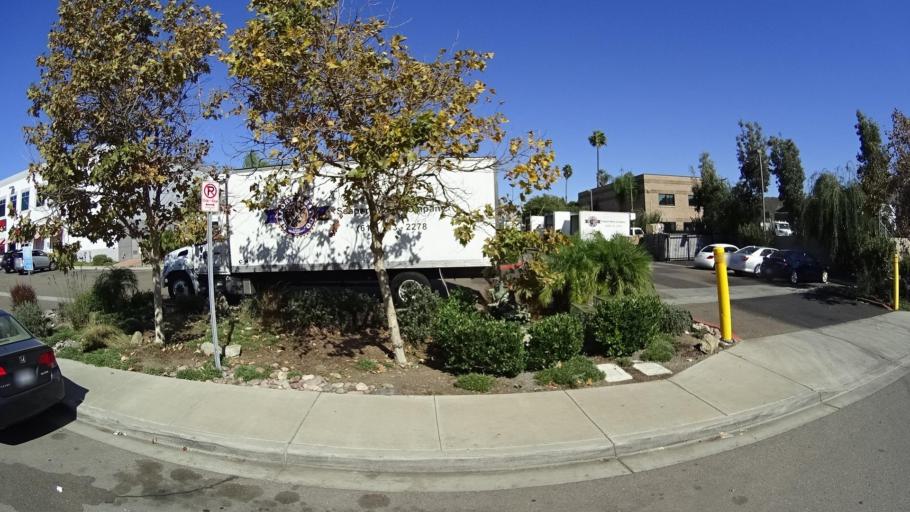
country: US
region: California
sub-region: San Diego County
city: La Presa
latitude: 32.7267
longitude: -116.9659
